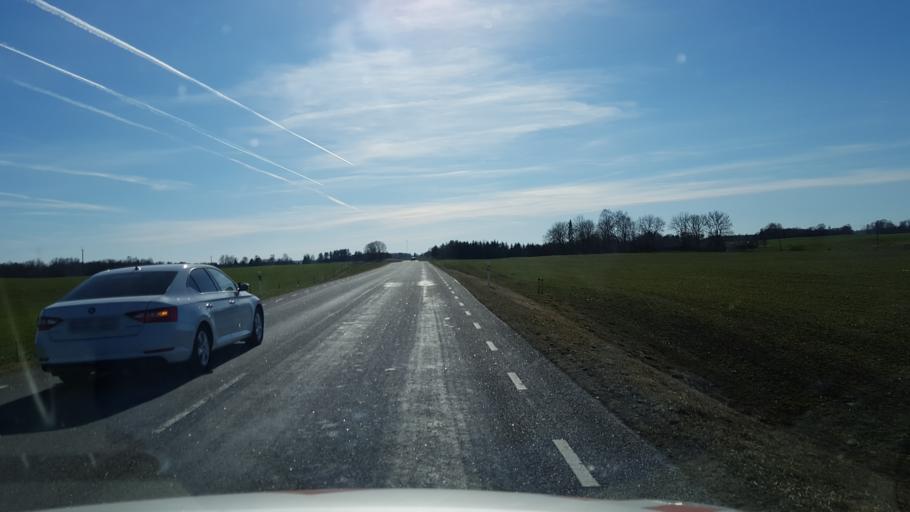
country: EE
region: Laeaene-Virumaa
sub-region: Vinni vald
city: Vinni
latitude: 59.3171
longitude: 26.4674
